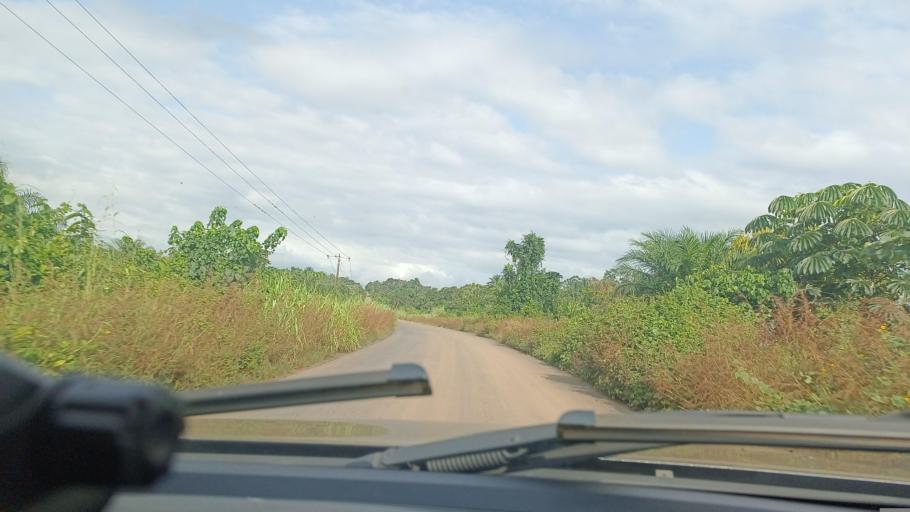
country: LR
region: Bomi
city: Tubmanburg
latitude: 6.7049
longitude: -10.9230
